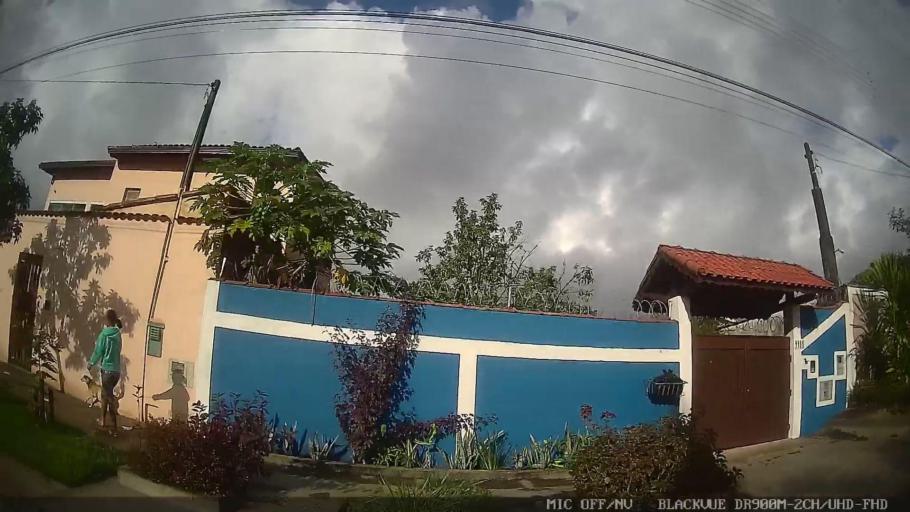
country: BR
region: Sao Paulo
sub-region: Itanhaem
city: Itanhaem
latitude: -24.1933
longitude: -46.8648
